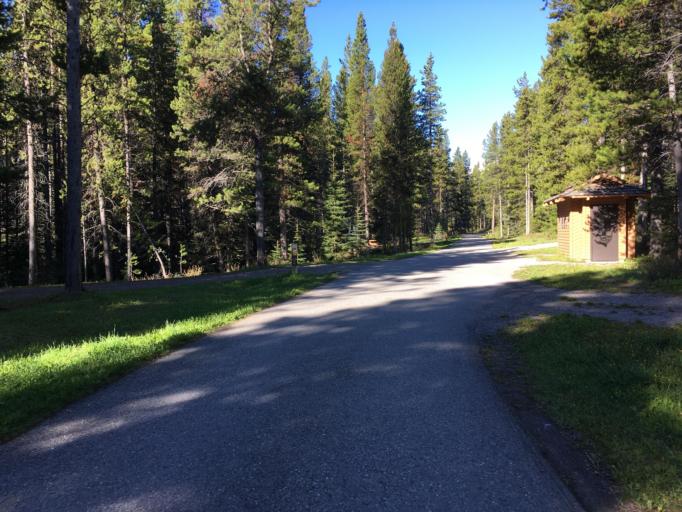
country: CA
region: Alberta
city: Canmore
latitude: 50.6336
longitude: -115.0978
